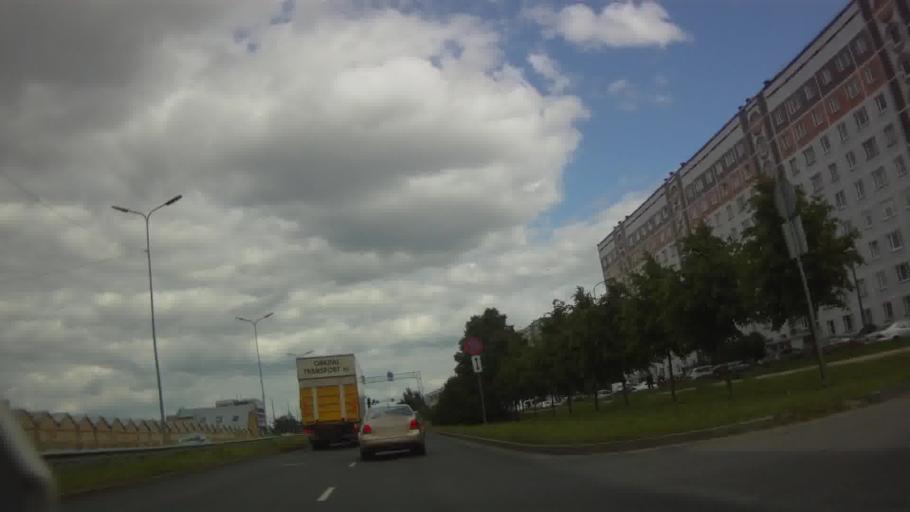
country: LV
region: Stopini
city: Ulbroka
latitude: 56.9454
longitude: 24.2146
